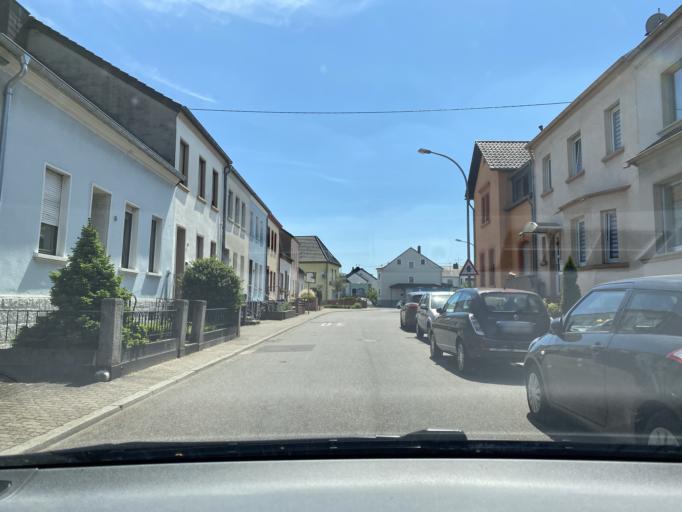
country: DE
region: Saarland
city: Saarlouis
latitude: 49.3260
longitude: 6.7732
